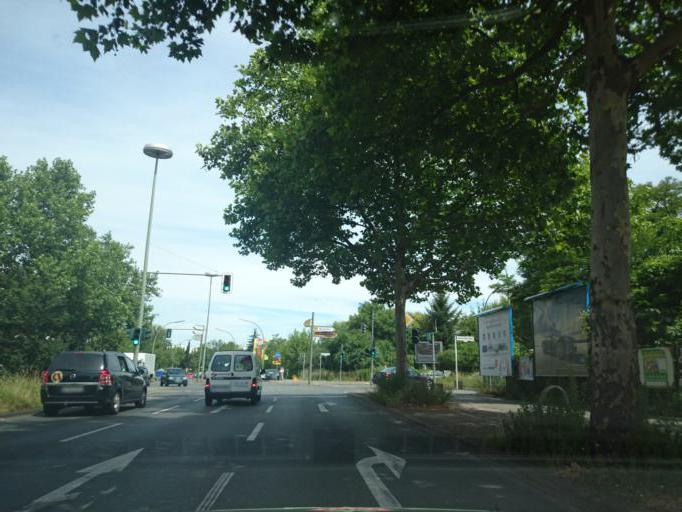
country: DE
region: Berlin
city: Marienfelde
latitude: 52.4133
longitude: 13.3620
